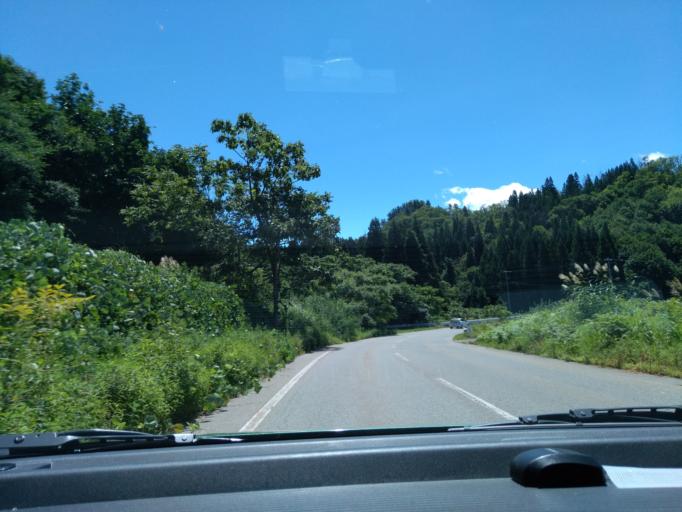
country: JP
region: Akita
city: Yokotemachi
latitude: 39.2477
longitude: 140.5677
